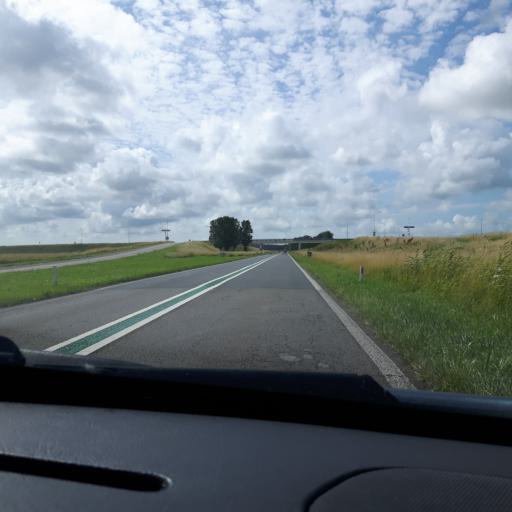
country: NL
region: Zeeland
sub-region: Gemeente Goes
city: Goes
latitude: 51.5783
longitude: 3.8117
